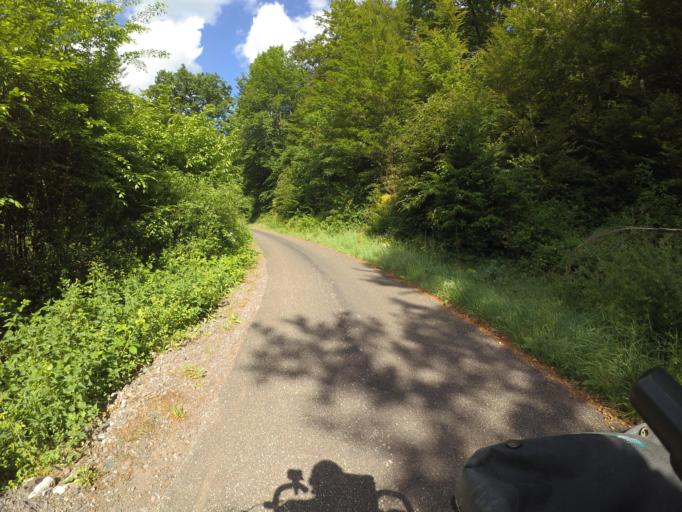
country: DE
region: Rheinland-Pfalz
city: Fischbach
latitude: 49.1121
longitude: 7.6972
